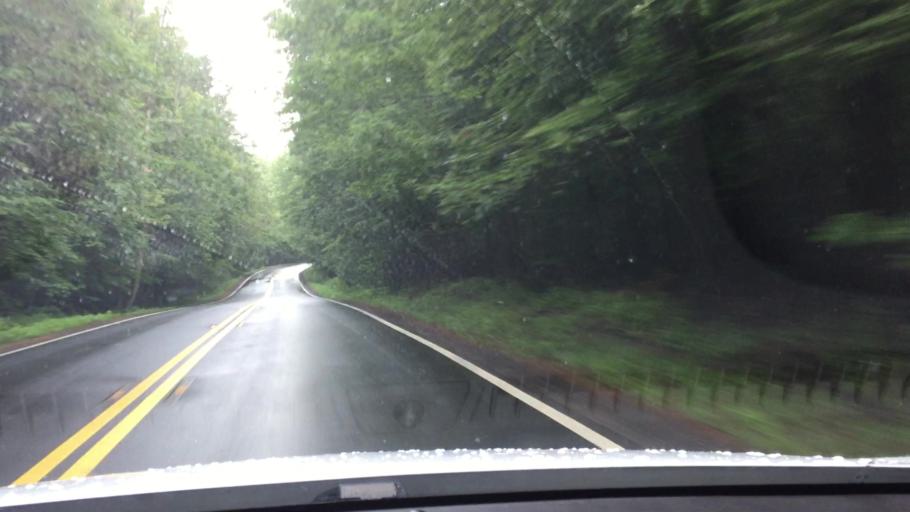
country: US
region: Massachusetts
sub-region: Berkshire County
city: Hinsdale
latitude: 42.4024
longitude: -73.1741
